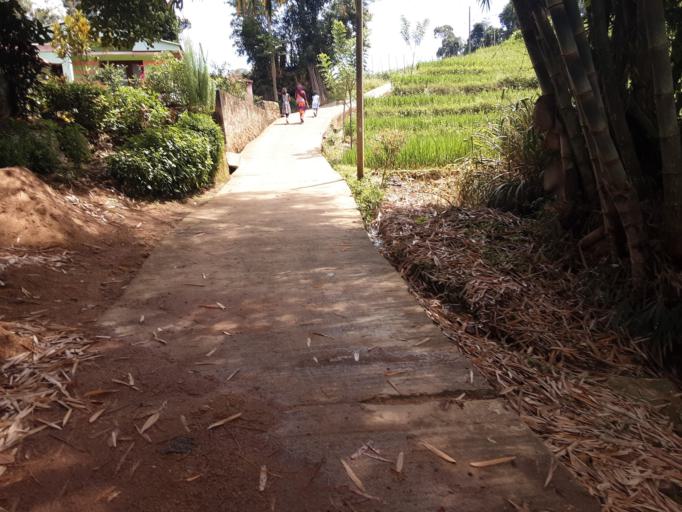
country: LK
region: Uva
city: Haputale
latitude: 6.8932
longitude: 80.9259
